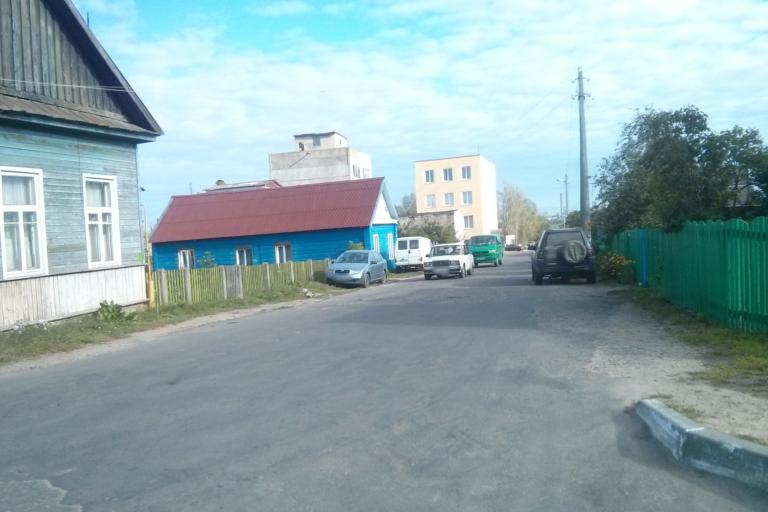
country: BY
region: Minsk
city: Chervyen'
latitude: 53.7140
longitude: 28.4202
